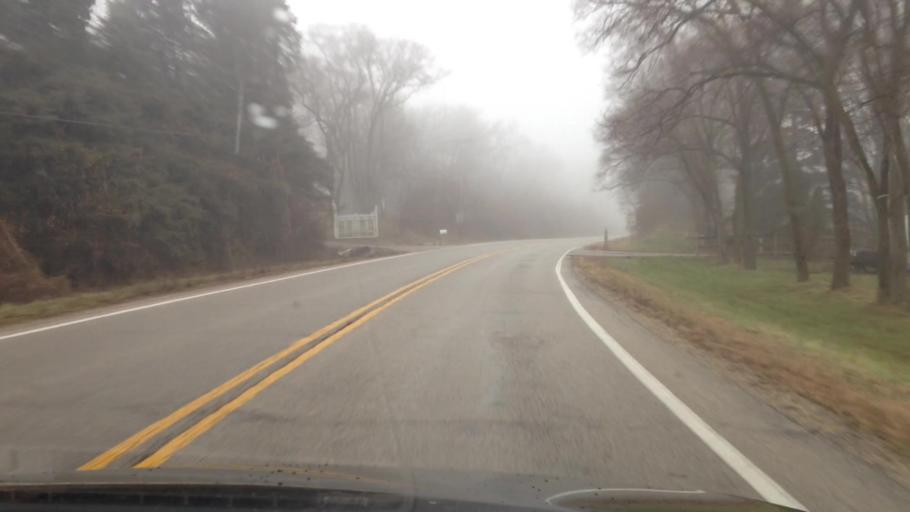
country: US
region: Illinois
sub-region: McHenry County
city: Hebron
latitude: 42.4808
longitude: -88.4424
